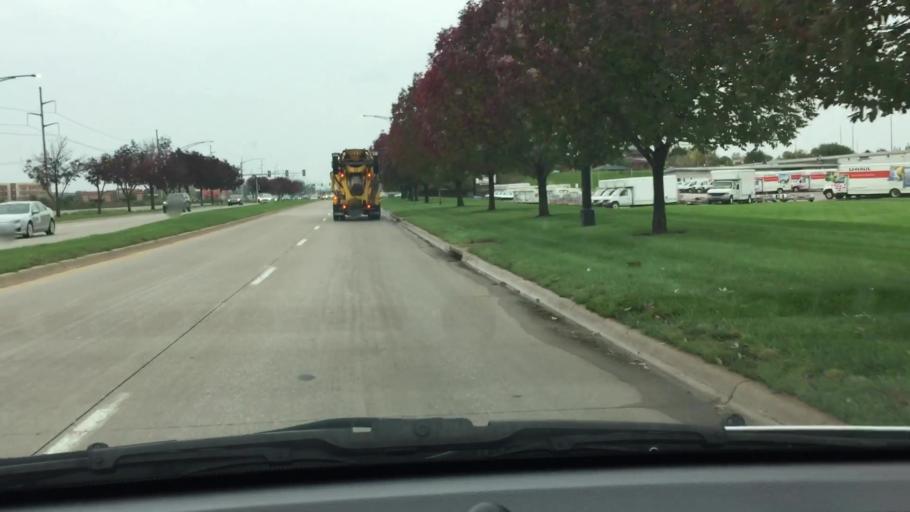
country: US
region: Iowa
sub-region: Johnson County
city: Coralville
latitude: 41.6862
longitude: -91.6043
